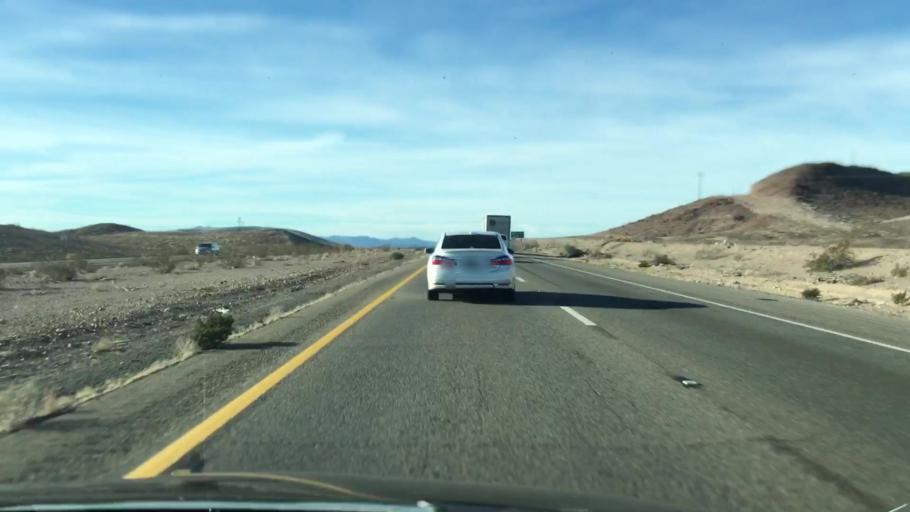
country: US
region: California
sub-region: San Bernardino County
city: Fort Irwin
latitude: 35.1402
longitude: -116.2058
